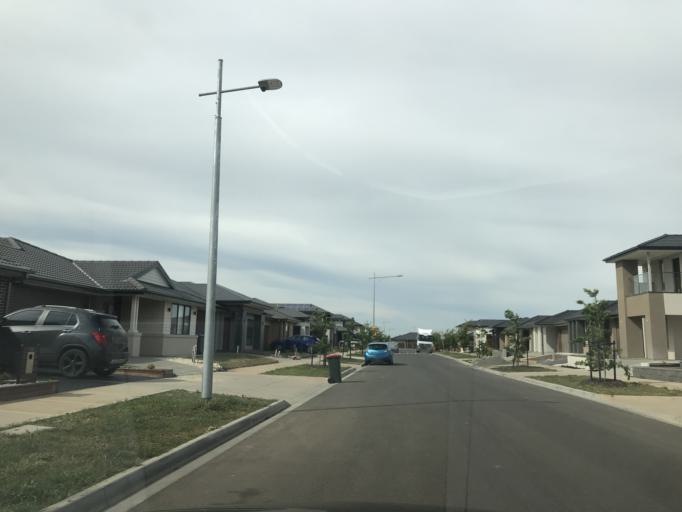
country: AU
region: Victoria
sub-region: Wyndham
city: Truganina
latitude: -37.8324
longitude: 144.7148
